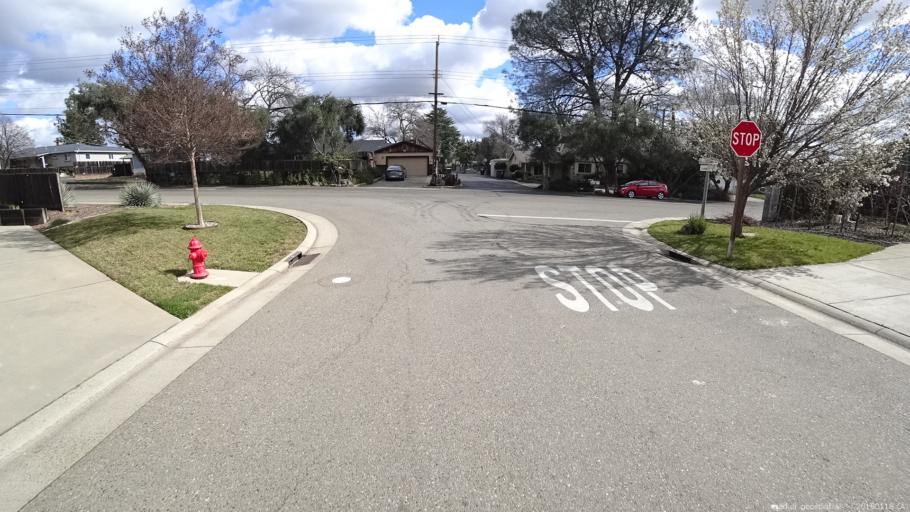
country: US
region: California
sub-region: Sacramento County
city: Orangevale
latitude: 38.6844
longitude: -121.2117
